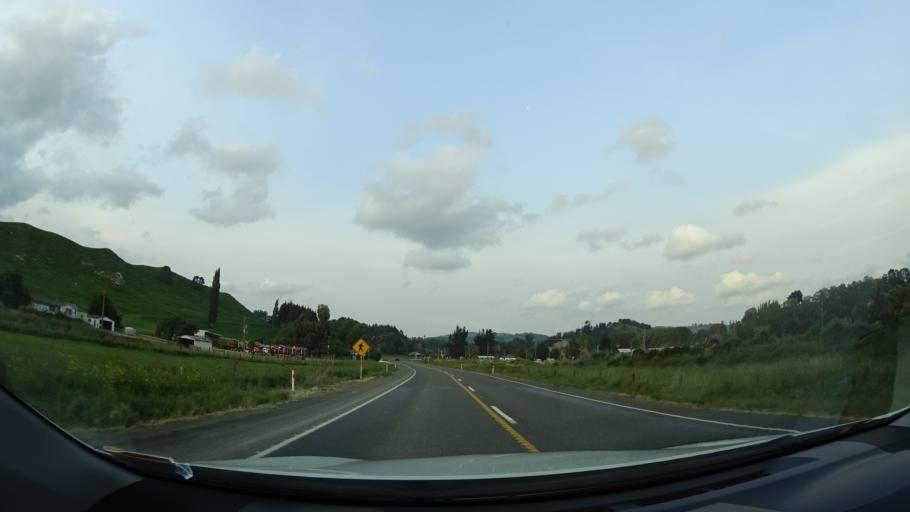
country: NZ
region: Manawatu-Wanganui
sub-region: Ruapehu District
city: Waiouru
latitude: -39.7353
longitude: 175.8424
